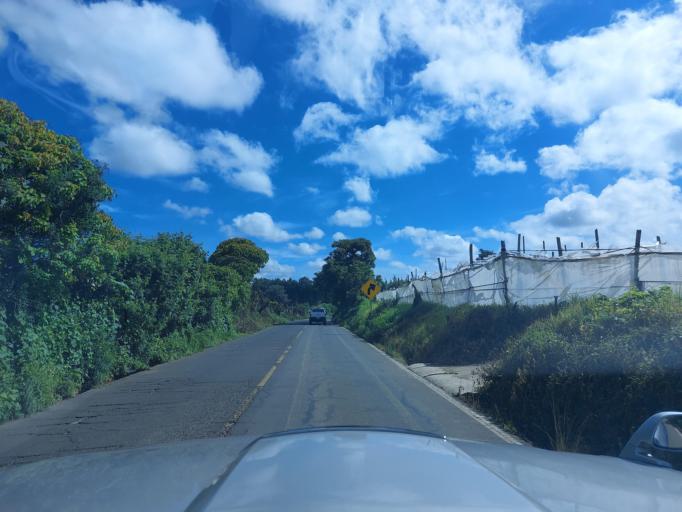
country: GT
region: Chimaltenango
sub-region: Municipio de Zaragoza
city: Zaragoza
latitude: 14.6673
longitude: -90.9007
